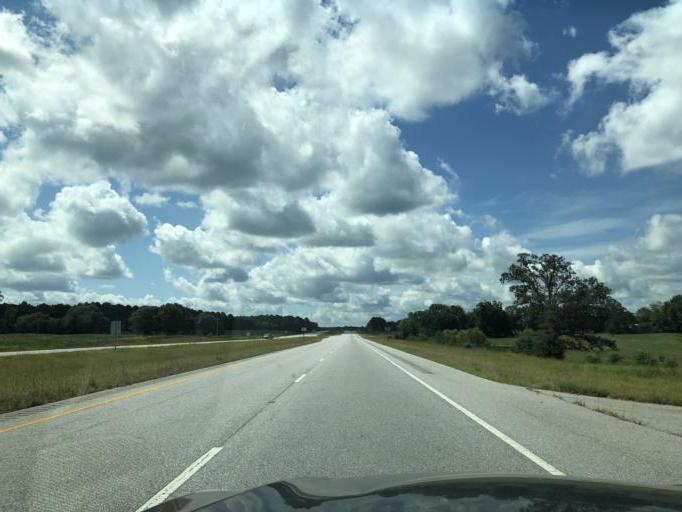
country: US
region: Alabama
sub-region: Barbour County
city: Eufaula
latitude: 32.0938
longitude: -85.1501
